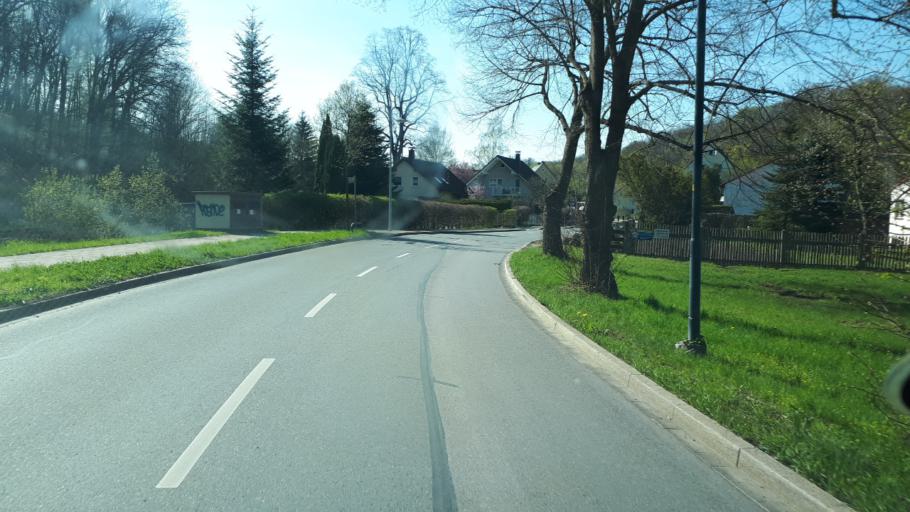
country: DE
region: Saxony
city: Chemnitz
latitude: 50.7842
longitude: 12.9641
